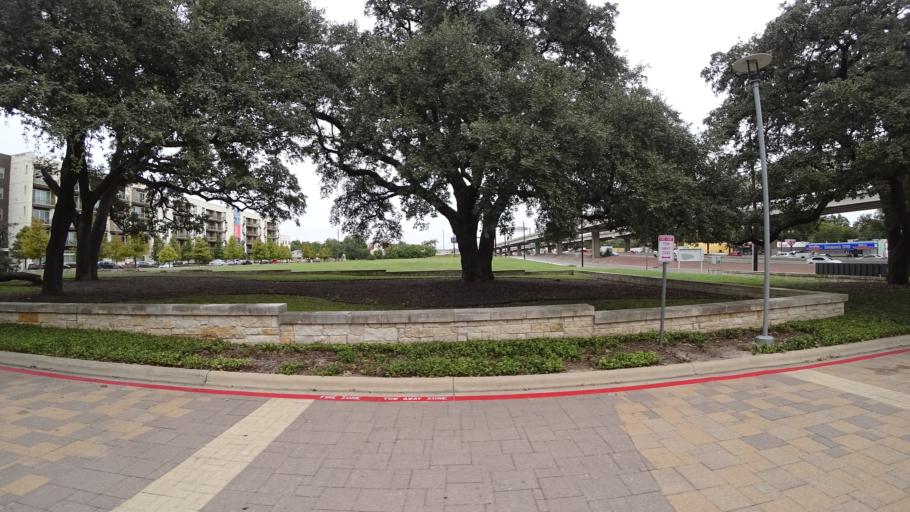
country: US
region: Texas
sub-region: Travis County
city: Austin
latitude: 30.2918
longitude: -97.7223
